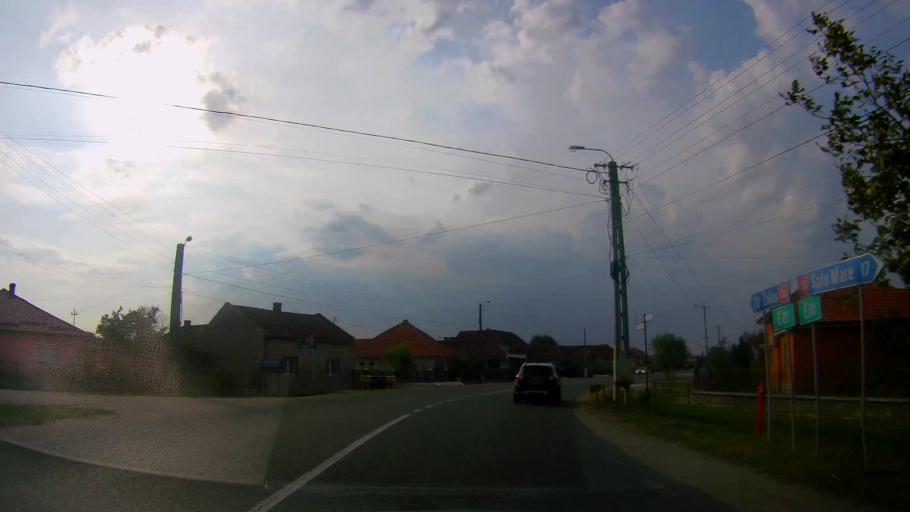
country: RO
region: Satu Mare
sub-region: Oras Ardud
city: Ardud
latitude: 47.6501
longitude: 22.8911
